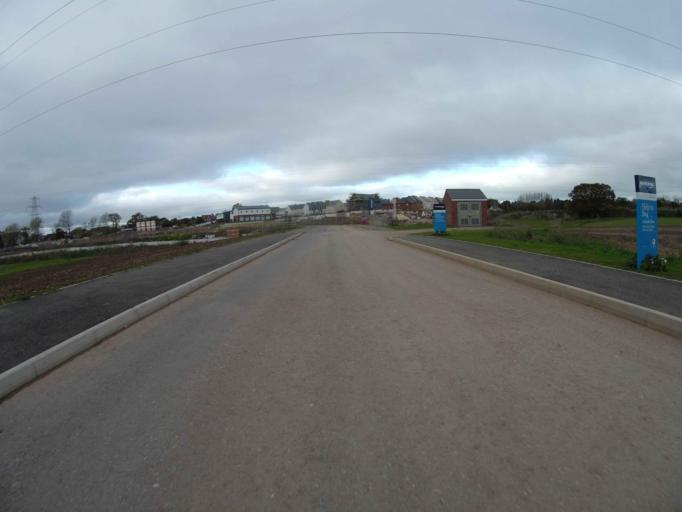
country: GB
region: England
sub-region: Devon
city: Topsham
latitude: 50.6952
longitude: -3.4785
